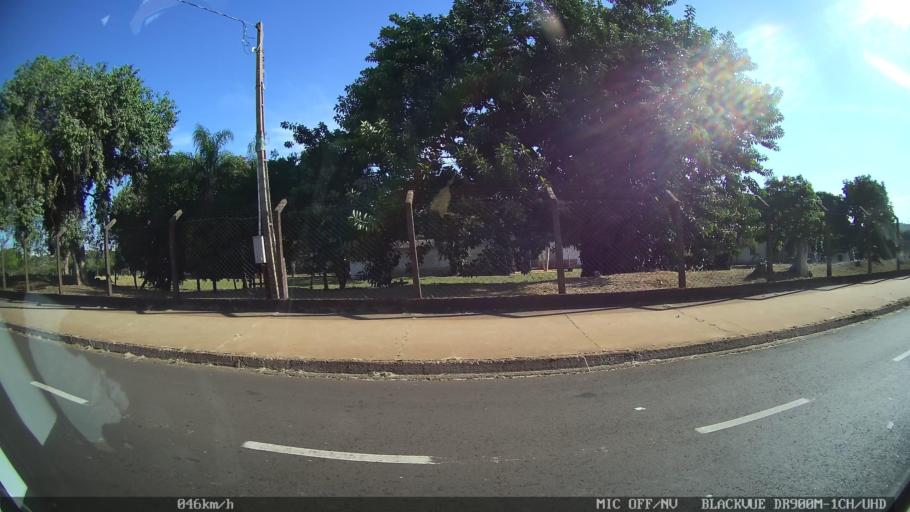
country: BR
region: Sao Paulo
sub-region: Franca
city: Franca
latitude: -20.5224
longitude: -47.4352
